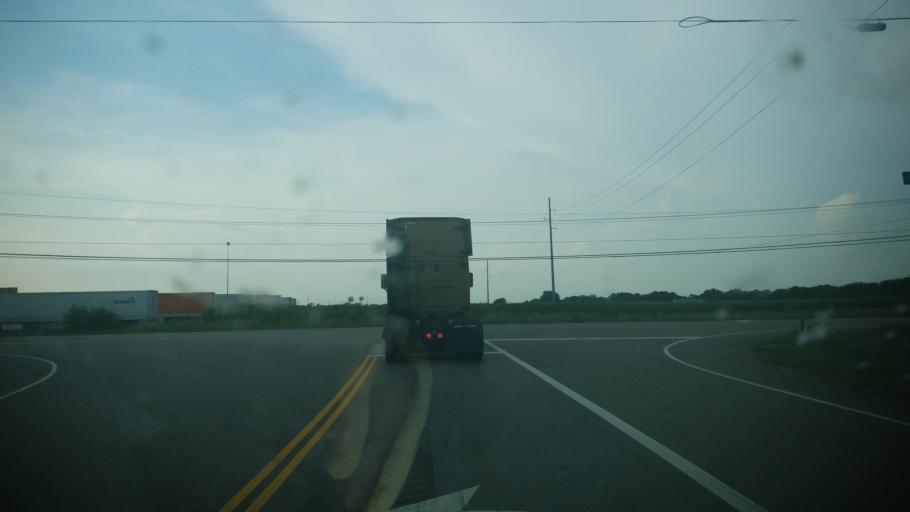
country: US
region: Ohio
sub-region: Pickaway County
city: Logan Elm Village
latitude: 39.5570
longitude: -82.9560
